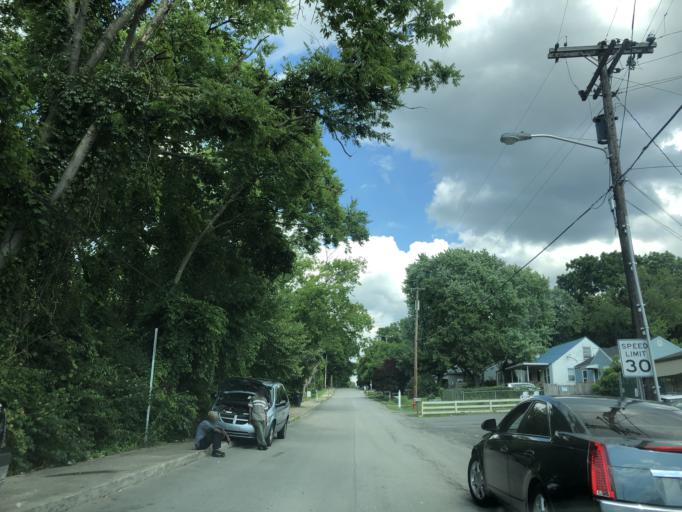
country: US
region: Tennessee
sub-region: Davidson County
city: Nashville
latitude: 36.2084
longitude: -86.7666
